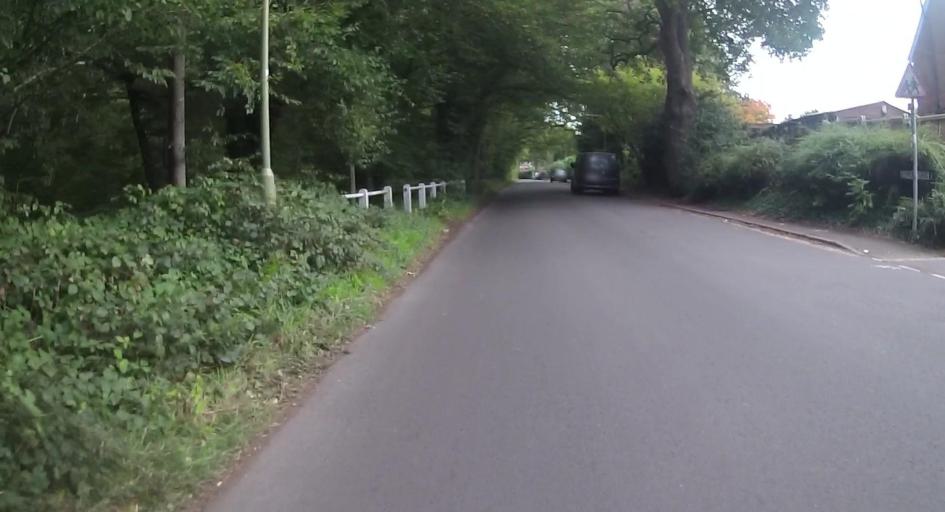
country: GB
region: England
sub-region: Hampshire
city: Hook
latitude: 51.2976
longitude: -0.9103
